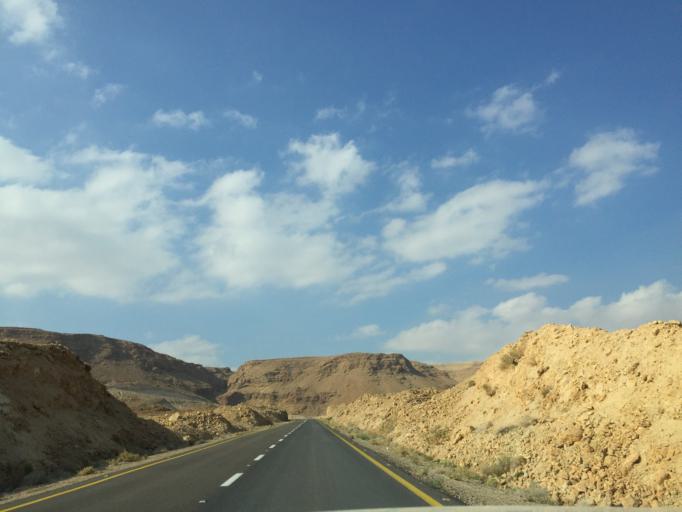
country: IL
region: Southern District
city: `En Boqeq
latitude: 31.3202
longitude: 35.3404
